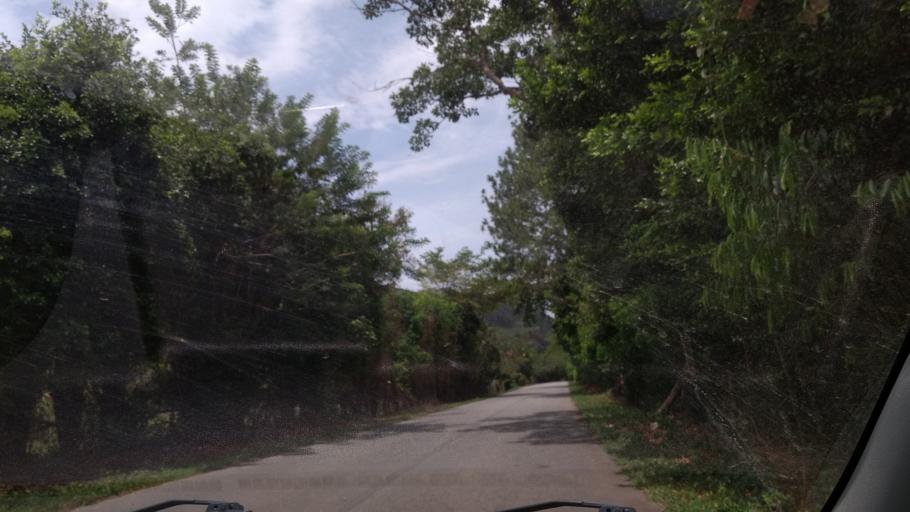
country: CO
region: Cauca
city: Buenos Aires
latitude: 3.0714
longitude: -76.6540
